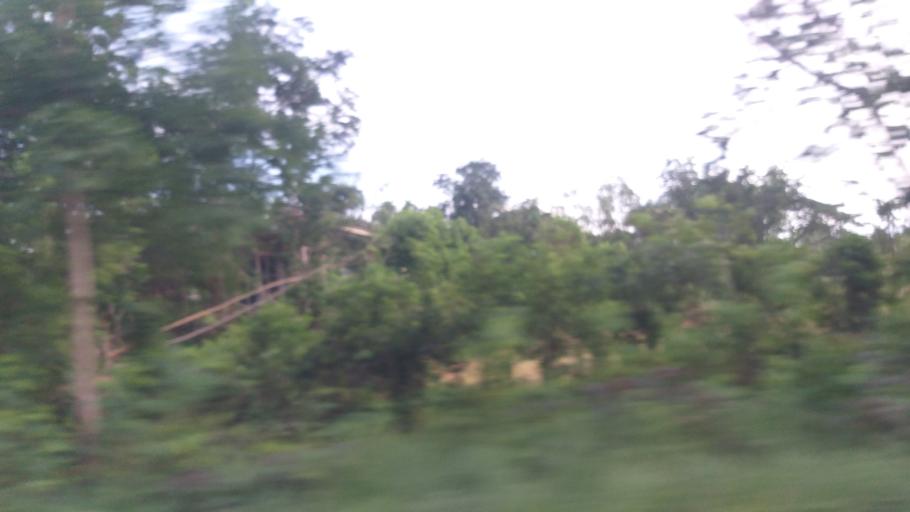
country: TH
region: Chaiyaphum
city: Phu Khiao
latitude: 16.3221
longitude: 102.2042
